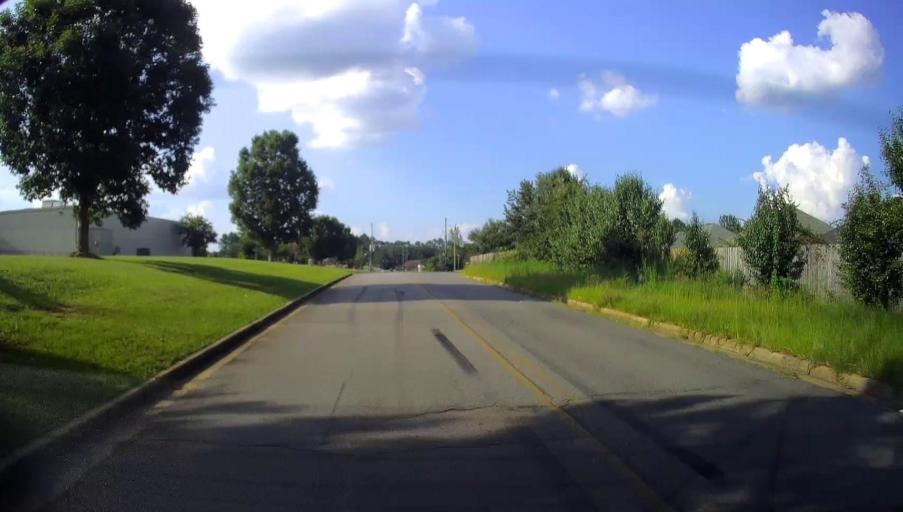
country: US
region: Georgia
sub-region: Houston County
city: Warner Robins
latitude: 32.5906
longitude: -83.6274
